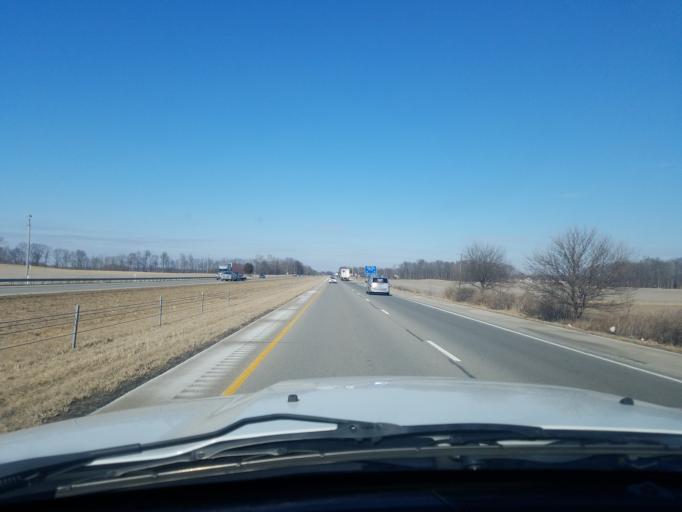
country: US
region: Indiana
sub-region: Bartholomew County
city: Lowell
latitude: 39.2519
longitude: -85.9544
